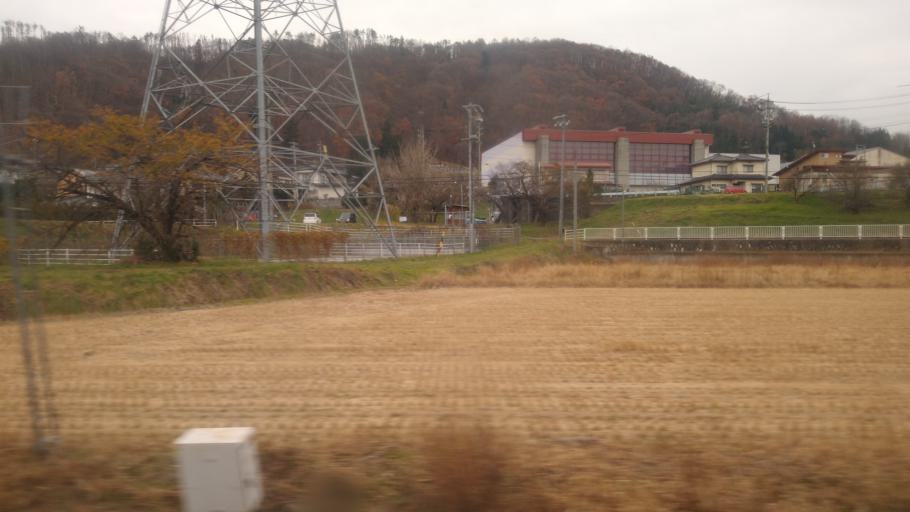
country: JP
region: Nagano
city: Hotaka
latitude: 36.3495
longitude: 137.9251
